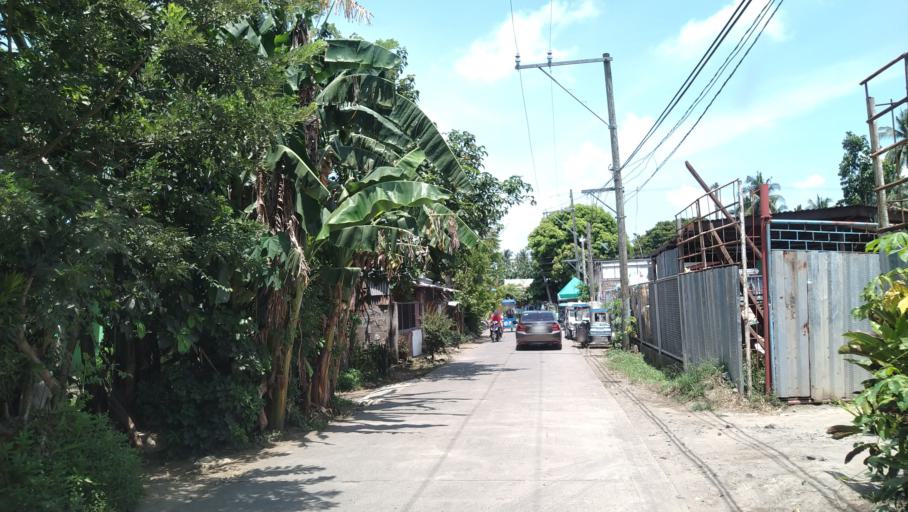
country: PH
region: Calabarzon
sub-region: Province of Laguna
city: Cabanbanan
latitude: 14.2432
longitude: 121.4041
